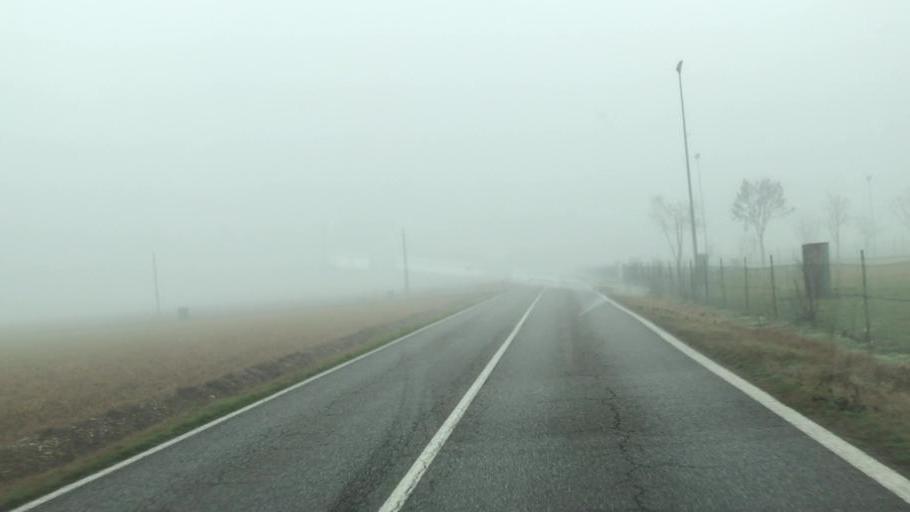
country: IT
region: Lombardy
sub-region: Provincia di Brescia
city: Novagli
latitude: 45.3836
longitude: 10.4096
